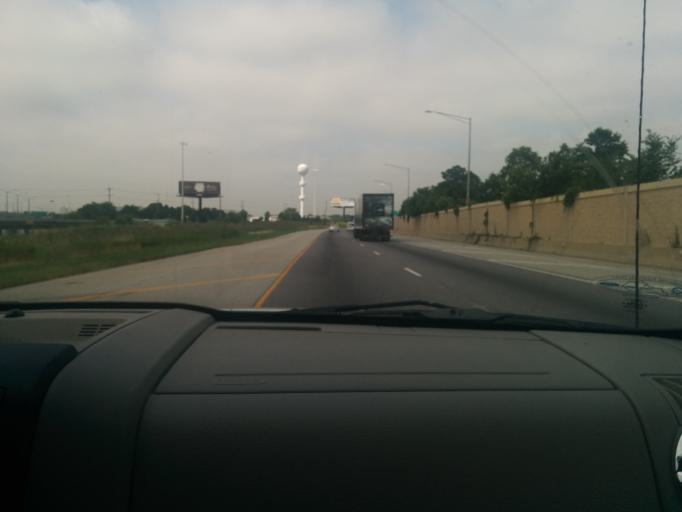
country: US
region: Illinois
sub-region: Cook County
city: Hillside
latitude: 41.8737
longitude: -87.9071
